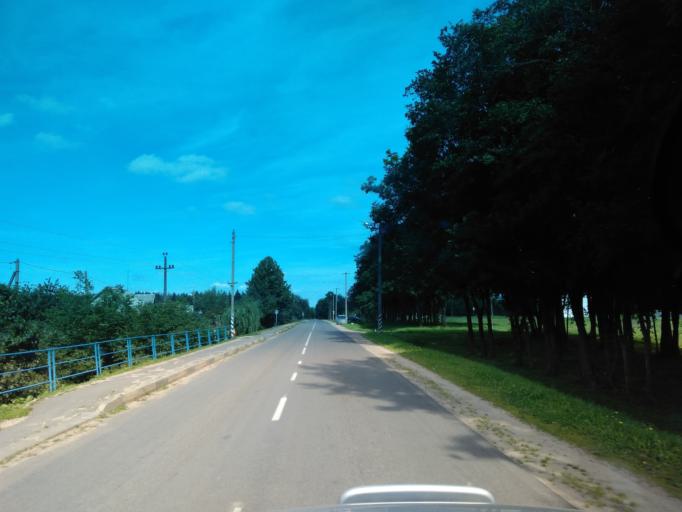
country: BY
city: Fanipol
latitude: 53.7462
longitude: 27.3376
